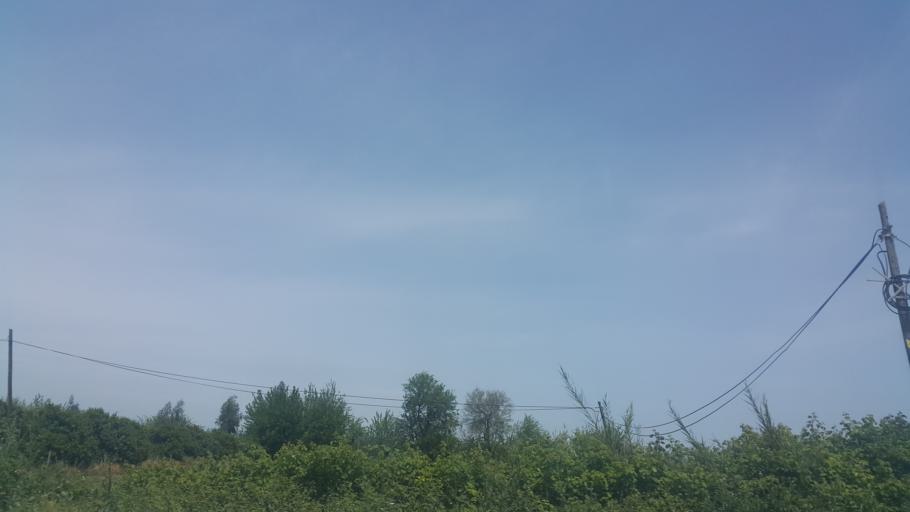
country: TR
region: Osmaniye
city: Toprakkale
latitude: 37.0635
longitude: 36.1079
